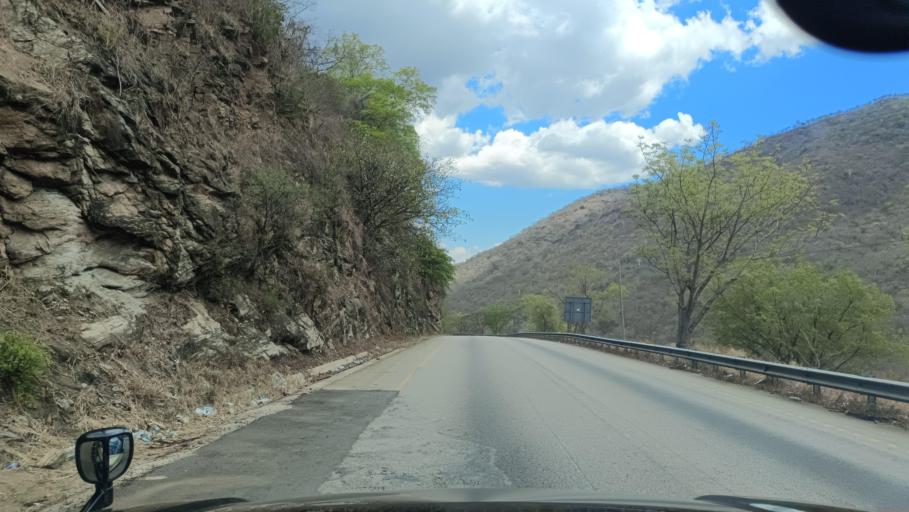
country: TZ
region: Morogoro
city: Kidatu
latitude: -7.5738
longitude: 36.7411
